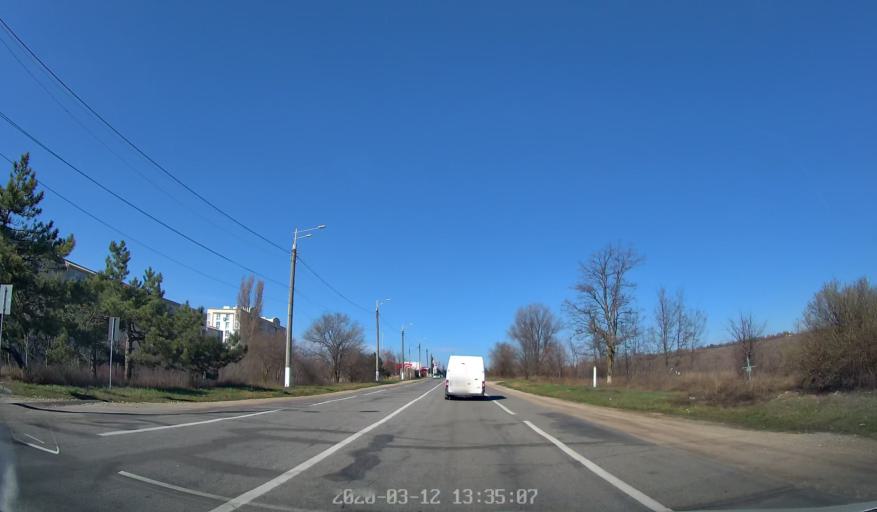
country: MD
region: Laloveni
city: Ialoveni
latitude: 46.9690
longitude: 28.7664
